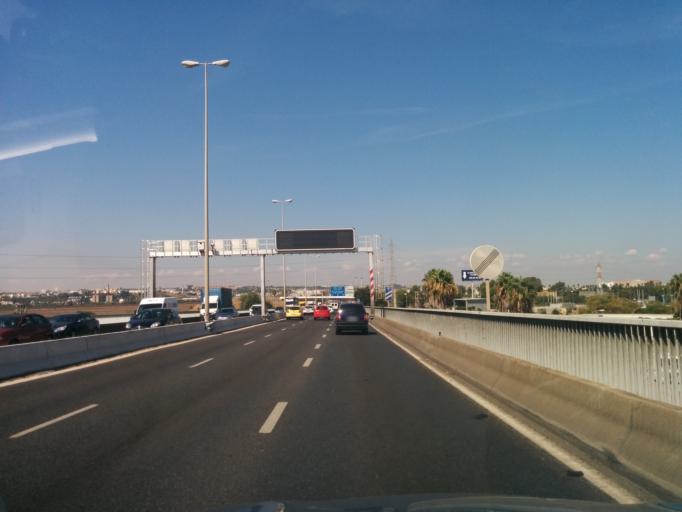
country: ES
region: Andalusia
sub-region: Provincia de Sevilla
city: Gelves
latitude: 37.3559
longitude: -6.0011
